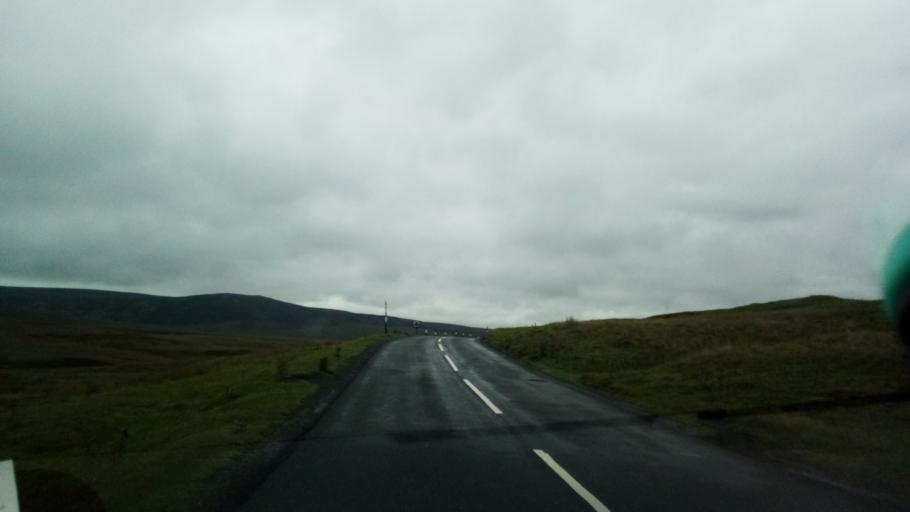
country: GB
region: England
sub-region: County Durham
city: Holwick
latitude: 54.5765
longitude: -2.2490
